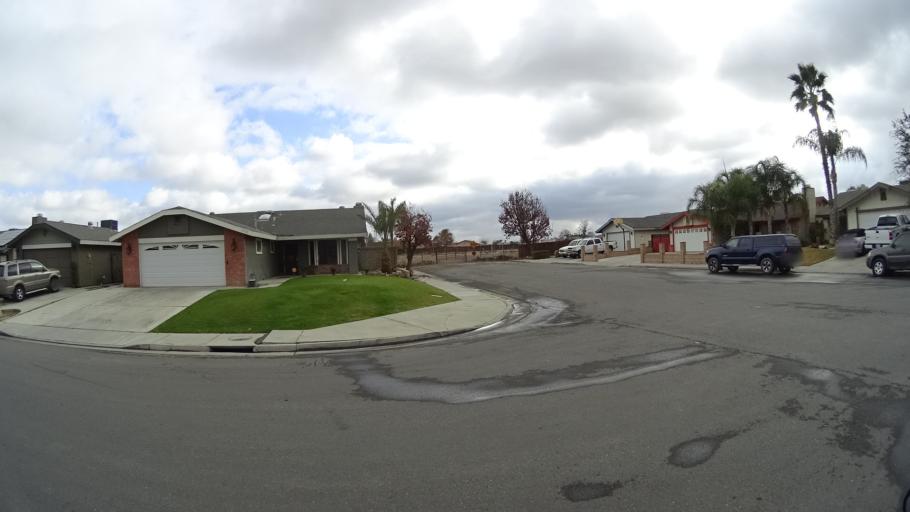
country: US
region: California
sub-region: Kern County
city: Greenfield
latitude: 35.2932
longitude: -119.0159
